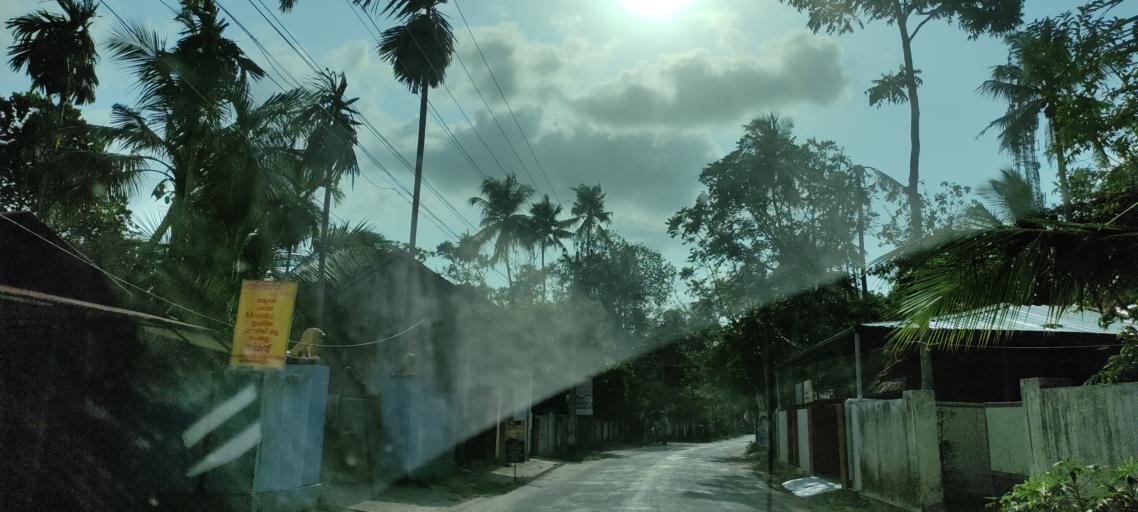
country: IN
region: Kerala
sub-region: Alappuzha
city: Vayalar
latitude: 9.6876
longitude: 76.3247
